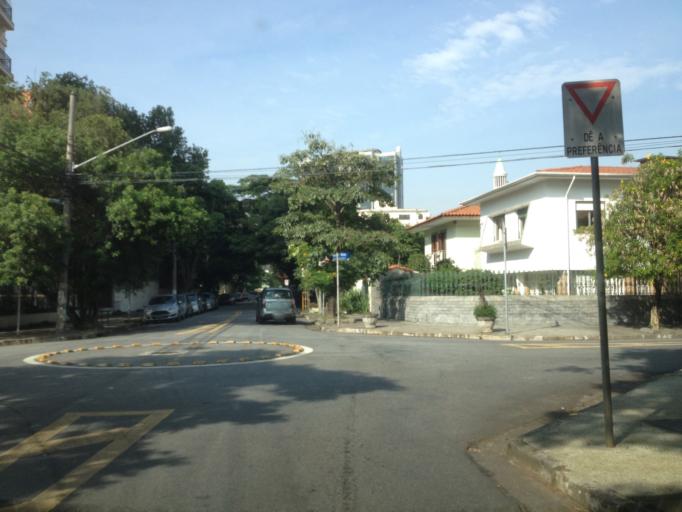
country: BR
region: Sao Paulo
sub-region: Sao Paulo
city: Sao Paulo
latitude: -23.5814
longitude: -46.6678
